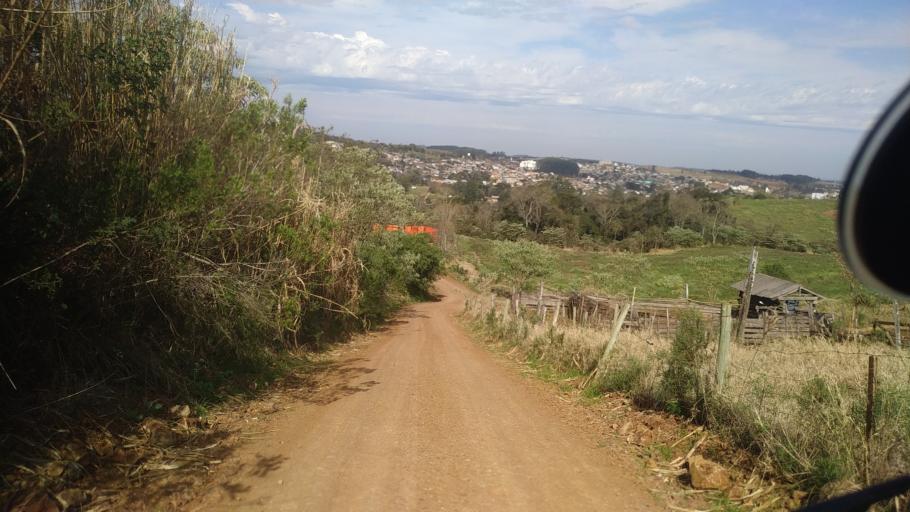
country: BR
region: Santa Catarina
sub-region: Chapeco
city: Chapeco
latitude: -27.1193
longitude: -52.5882
